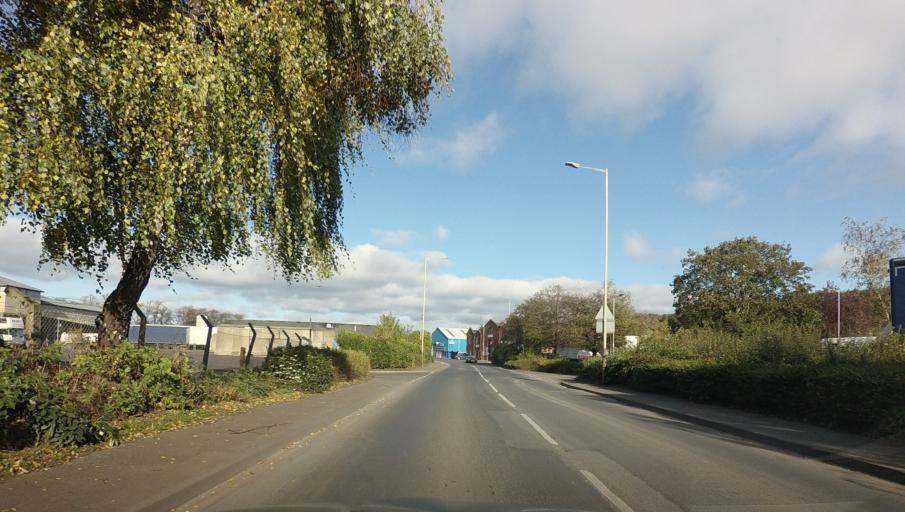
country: GB
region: Scotland
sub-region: Perth and Kinross
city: Perth
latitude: 56.3834
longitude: -3.4278
